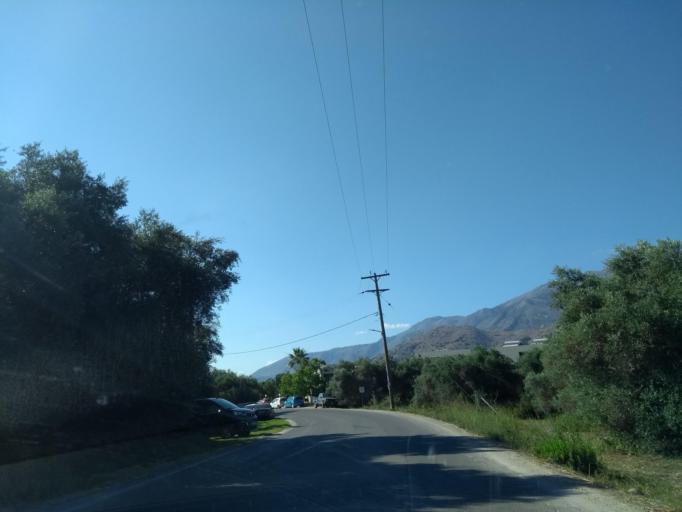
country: GR
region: Crete
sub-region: Nomos Chanias
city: Georgioupolis
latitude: 35.3680
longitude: 24.2539
